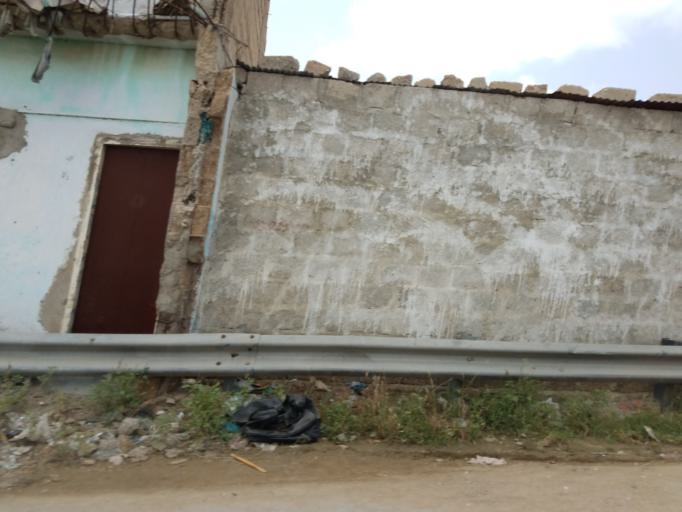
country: PK
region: Sindh
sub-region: Karachi District
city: Karachi
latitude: 24.9421
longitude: 67.0885
